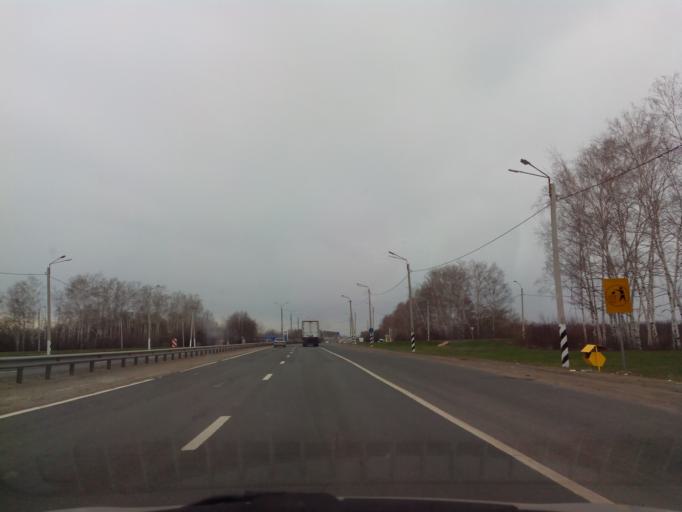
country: RU
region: Tambov
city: Komsomolets
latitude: 52.7338
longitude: 41.2940
